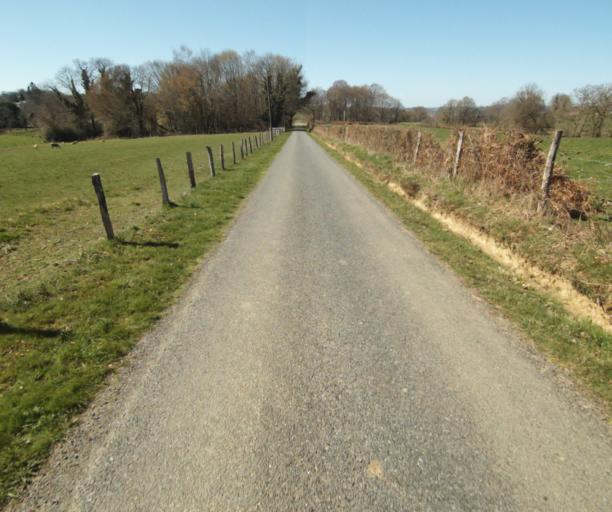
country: FR
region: Limousin
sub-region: Departement de la Correze
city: Uzerche
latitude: 45.3974
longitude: 1.6311
